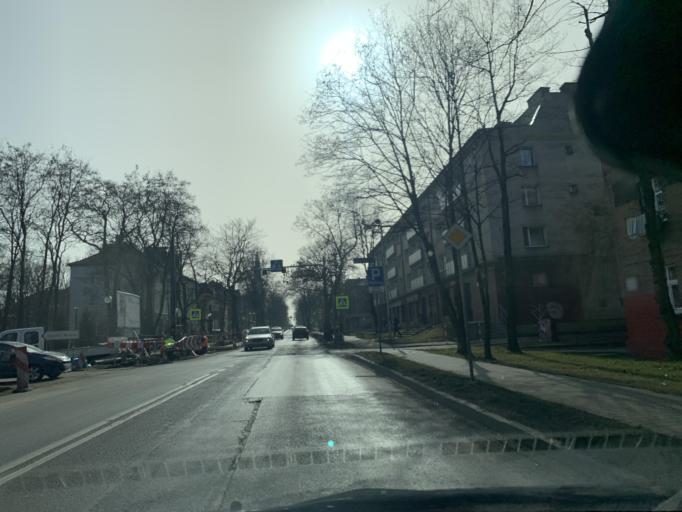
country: PL
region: Silesian Voivodeship
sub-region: Swietochlowice
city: Swietochlowice
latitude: 50.3156
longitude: 18.8875
